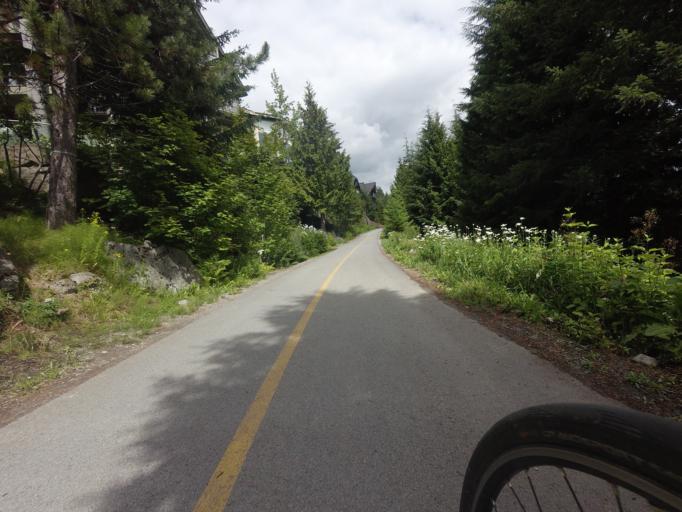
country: CA
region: British Columbia
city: Whistler
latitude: 50.1138
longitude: -122.9684
